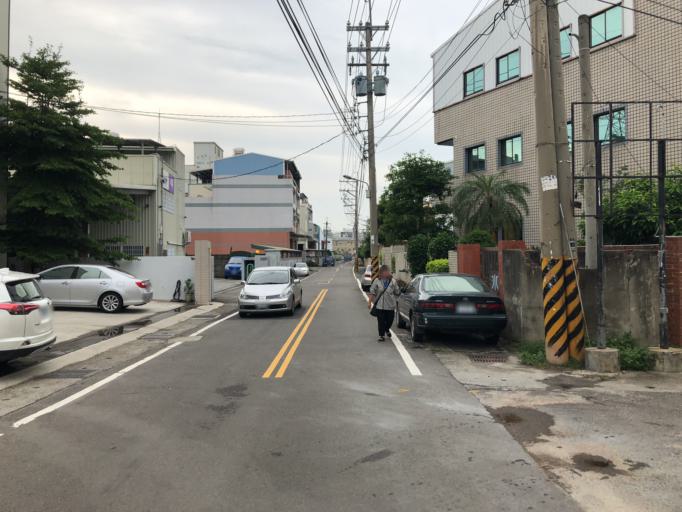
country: TW
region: Taiwan
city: Zhongxing New Village
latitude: 24.0470
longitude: 120.6917
